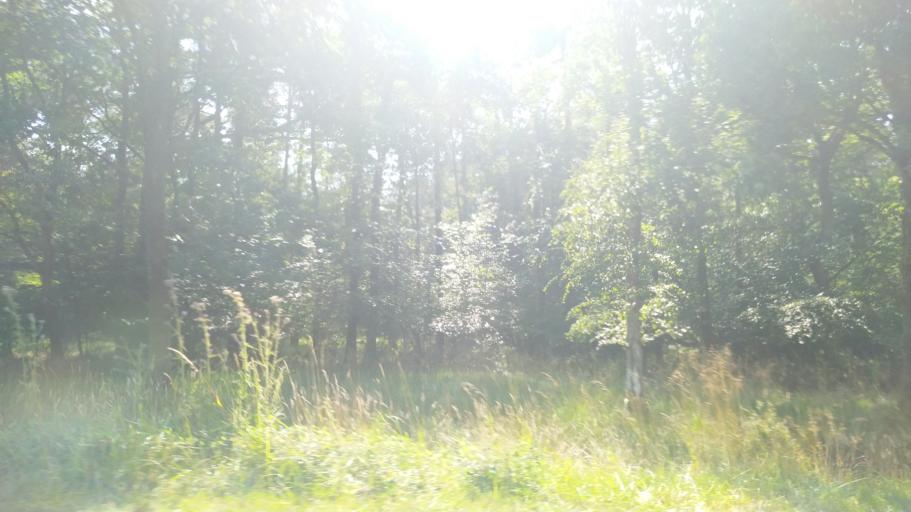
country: GB
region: England
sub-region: Hampshire
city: Totton
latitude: 50.8937
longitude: -1.5319
